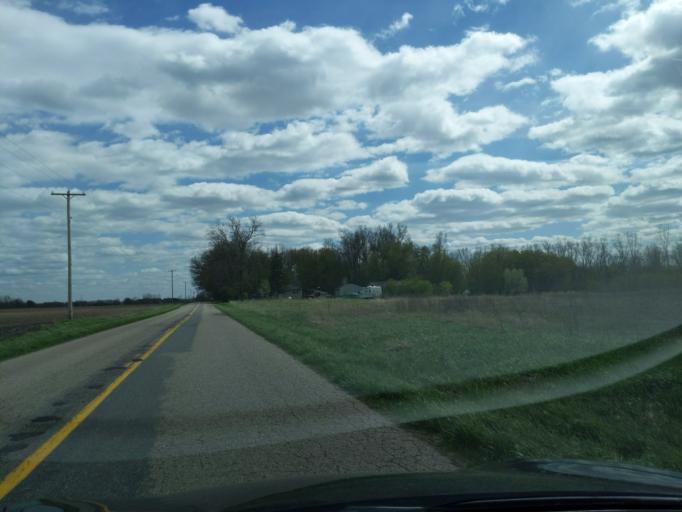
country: US
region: Michigan
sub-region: Ingham County
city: Mason
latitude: 42.5293
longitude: -84.5421
